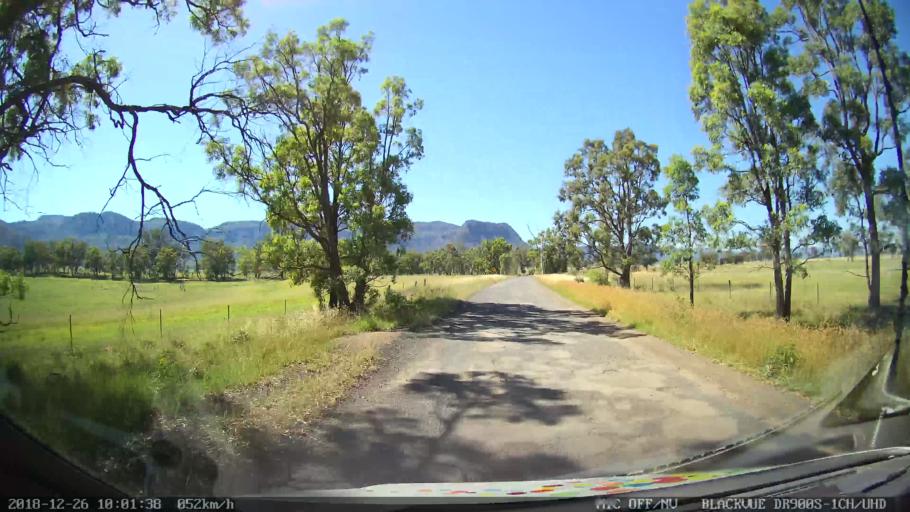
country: AU
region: New South Wales
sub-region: Mid-Western Regional
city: Kandos
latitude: -33.0485
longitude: 150.2224
